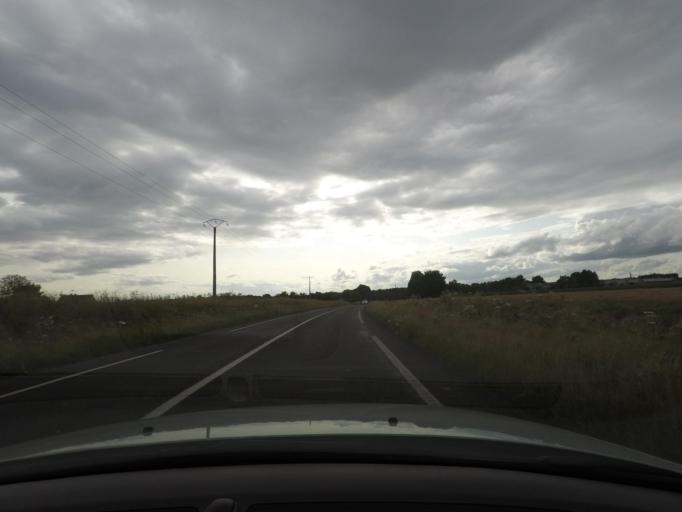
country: FR
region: Haute-Normandie
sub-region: Departement de la Seine-Maritime
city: Ymare
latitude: 49.3556
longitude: 1.1792
